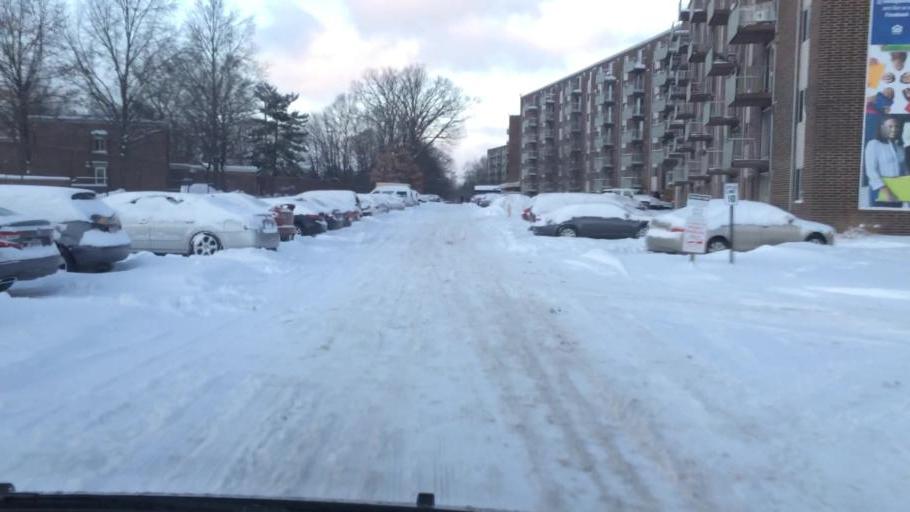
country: US
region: Ohio
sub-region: Portage County
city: Kent
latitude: 41.1453
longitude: -81.3337
